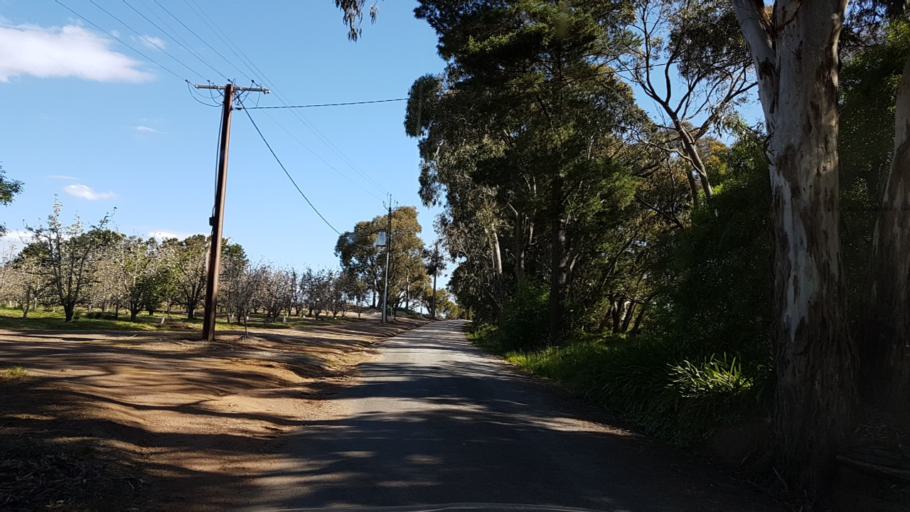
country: AU
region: South Australia
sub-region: Tea Tree Gully
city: Hope Valley
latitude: -34.8481
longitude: 138.7671
